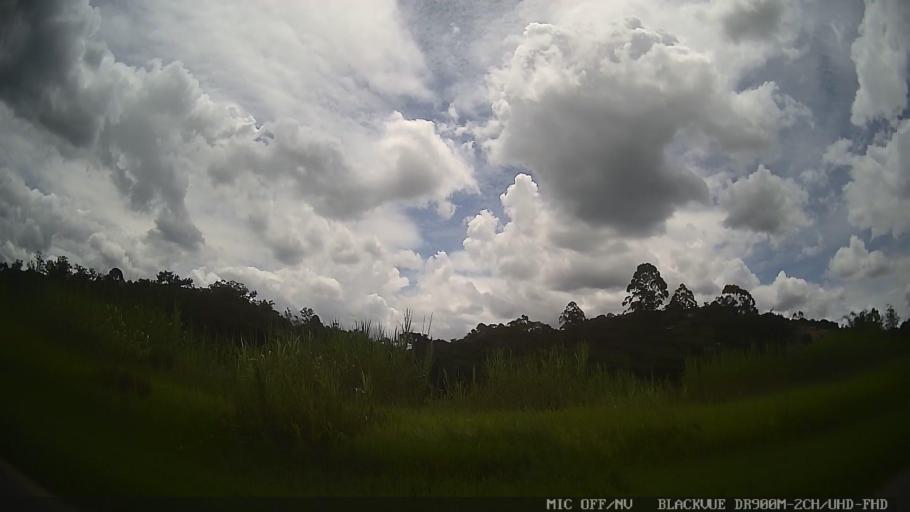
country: BR
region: Sao Paulo
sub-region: Suzano
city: Suzano
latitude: -23.6165
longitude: -46.3154
